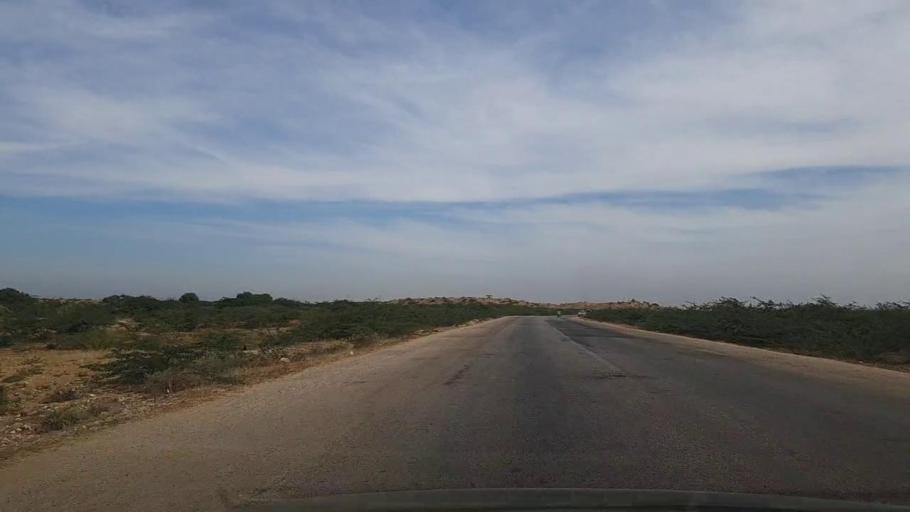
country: PK
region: Sindh
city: Daro Mehar
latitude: 24.8768
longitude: 68.0444
